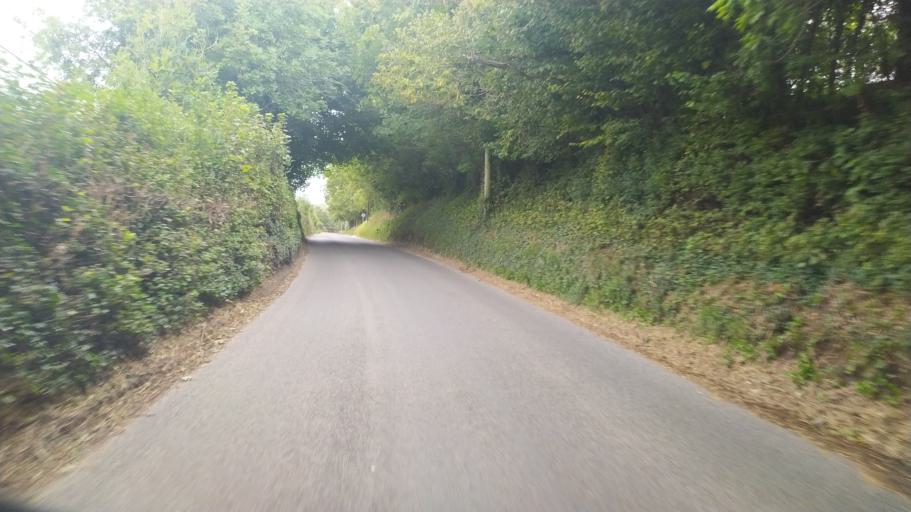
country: GB
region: England
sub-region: Dorset
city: Dorchester
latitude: 50.7885
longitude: -2.4146
